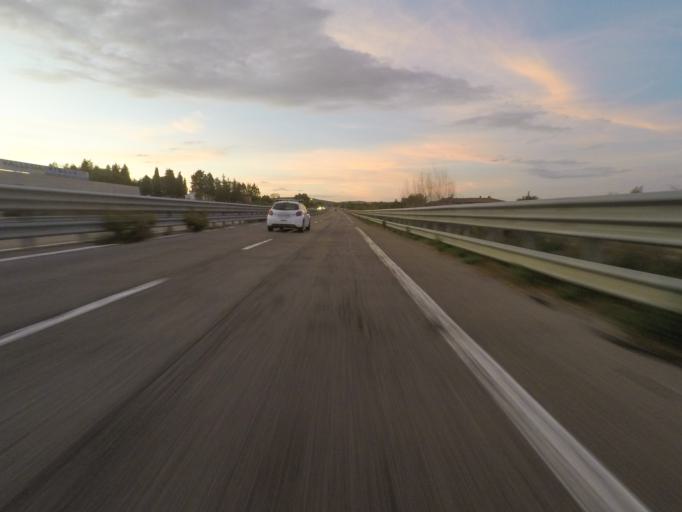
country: IT
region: Tuscany
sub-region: Provincia di Siena
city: Sinalunga
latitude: 43.2382
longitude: 11.7260
